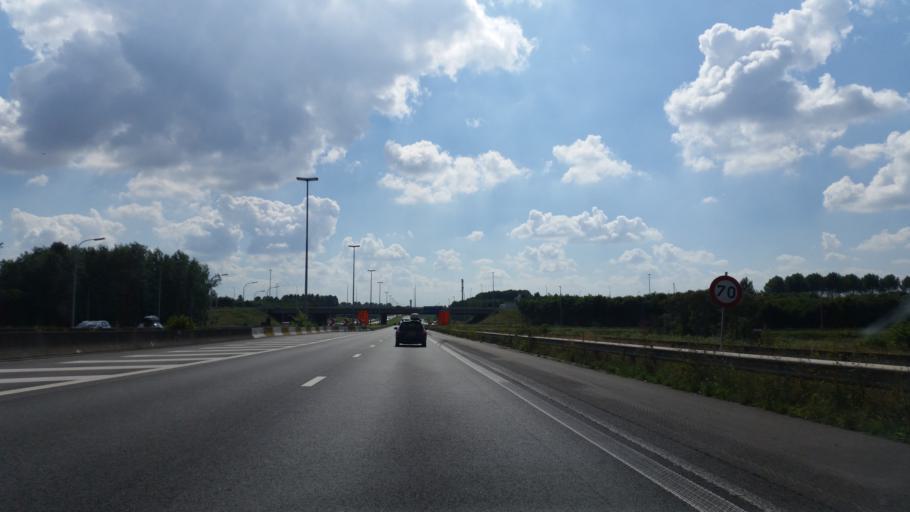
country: BE
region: Flanders
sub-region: Provincie West-Vlaanderen
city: Kortrijk
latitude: 50.7914
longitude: 3.2341
